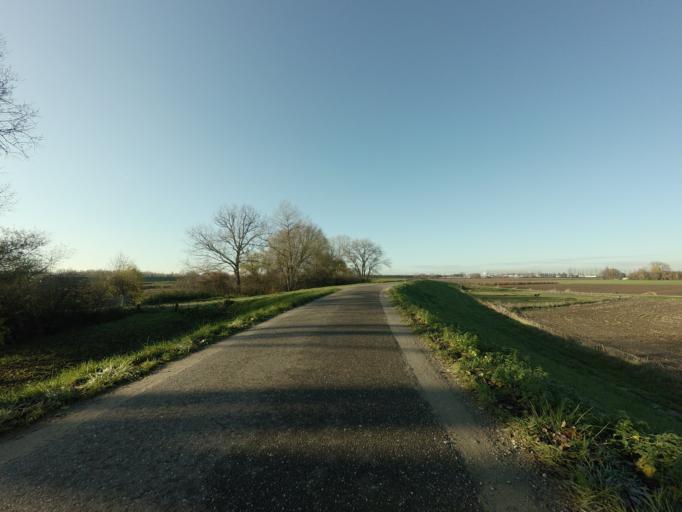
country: NL
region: Gelderland
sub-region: Gemeente Maasdriel
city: Hedel
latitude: 51.7460
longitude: 5.3026
